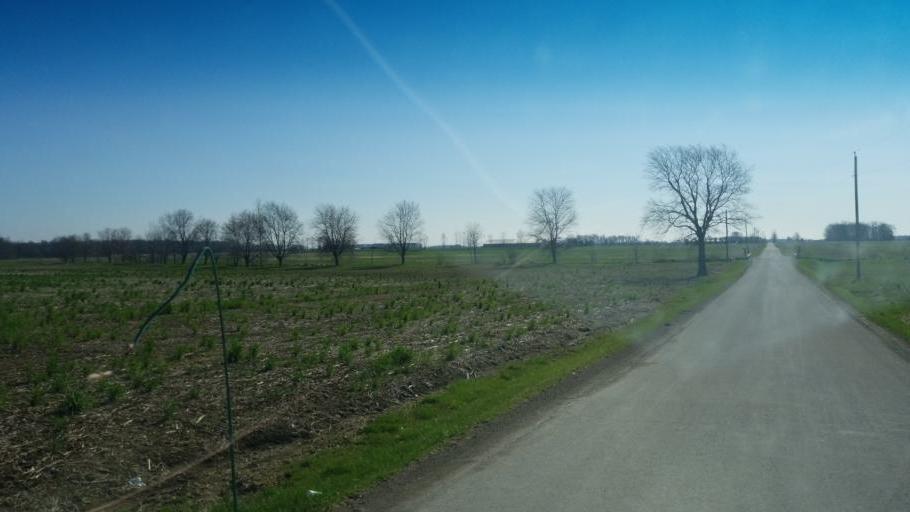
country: US
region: Ohio
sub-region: Hardin County
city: Kenton
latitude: 40.7021
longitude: -83.5378
